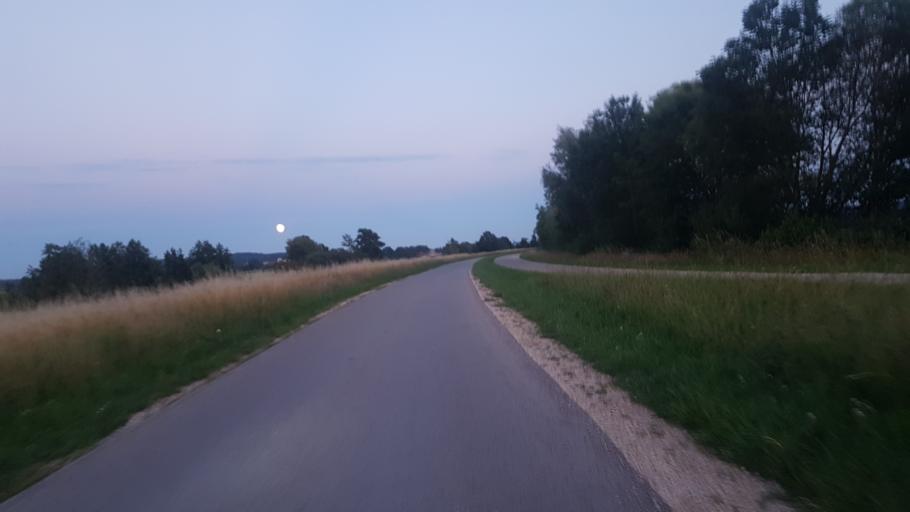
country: DE
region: Bavaria
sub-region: Regierungsbezirk Mittelfranken
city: Muhr am See
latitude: 49.1407
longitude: 10.7320
